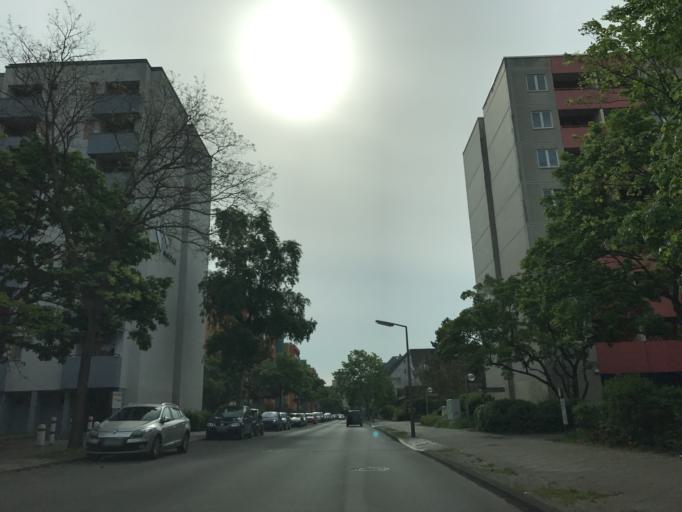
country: DE
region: Berlin
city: Wilhelmstadt
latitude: 52.5239
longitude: 13.1682
